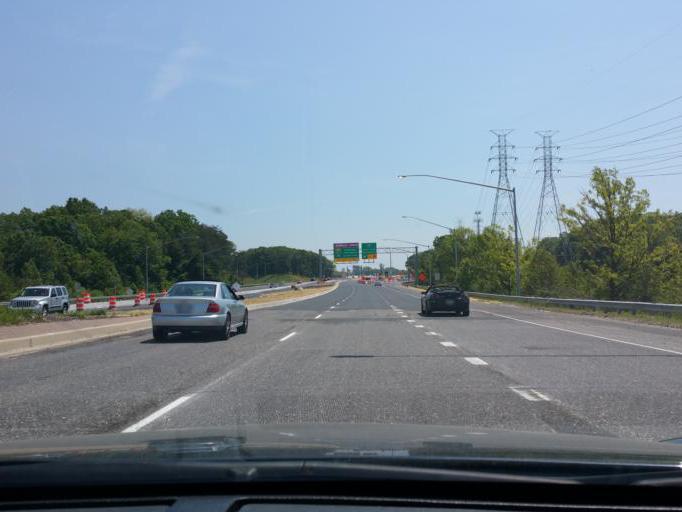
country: US
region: Maryland
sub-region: Baltimore County
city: White Marsh
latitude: 39.3794
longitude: -76.4581
